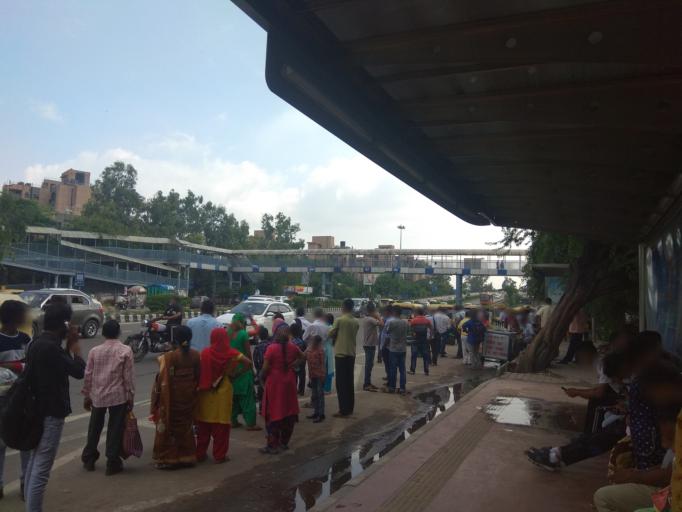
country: IN
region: NCT
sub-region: New Delhi
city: New Delhi
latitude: 28.5693
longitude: 77.2539
